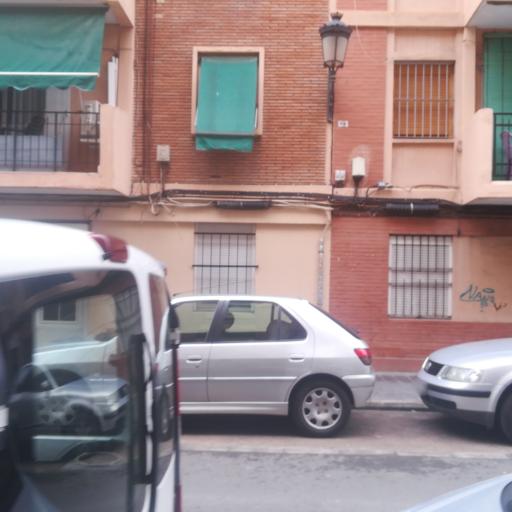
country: ES
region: Valencia
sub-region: Provincia de Valencia
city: Valencia
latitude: 39.4552
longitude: -0.3878
